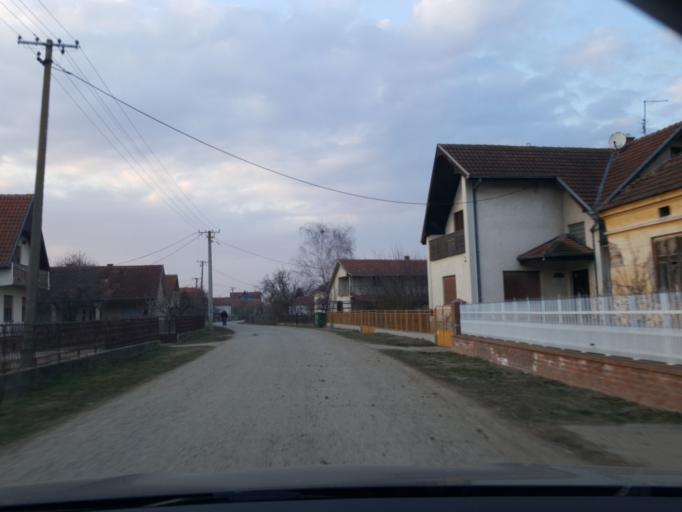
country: RS
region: Central Serbia
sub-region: Nisavski Okrug
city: Aleksinac
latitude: 43.5555
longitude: 21.6528
